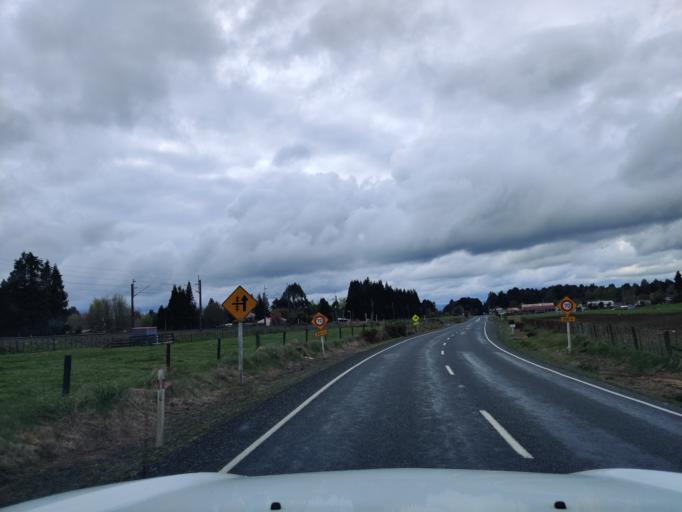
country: NZ
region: Waikato
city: Turangi
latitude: -39.0039
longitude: 175.3766
